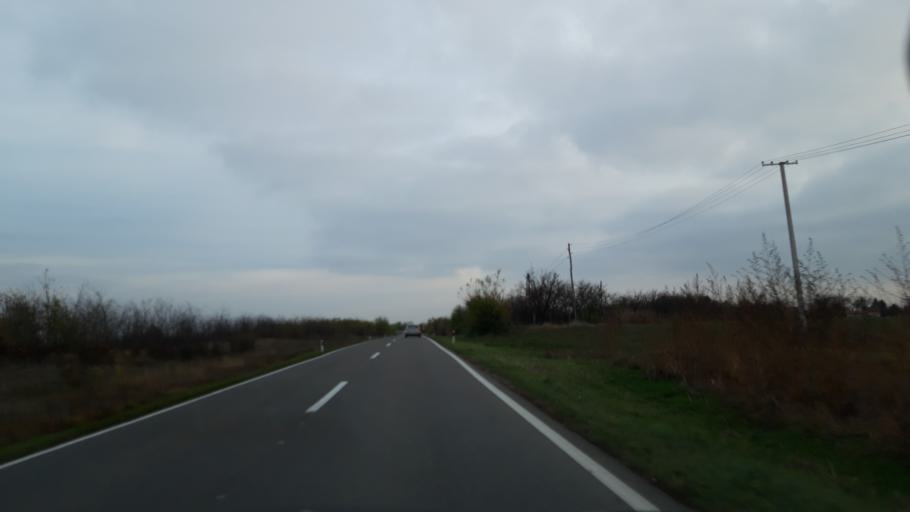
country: RS
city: Sanad
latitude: 45.9695
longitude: 20.1234
